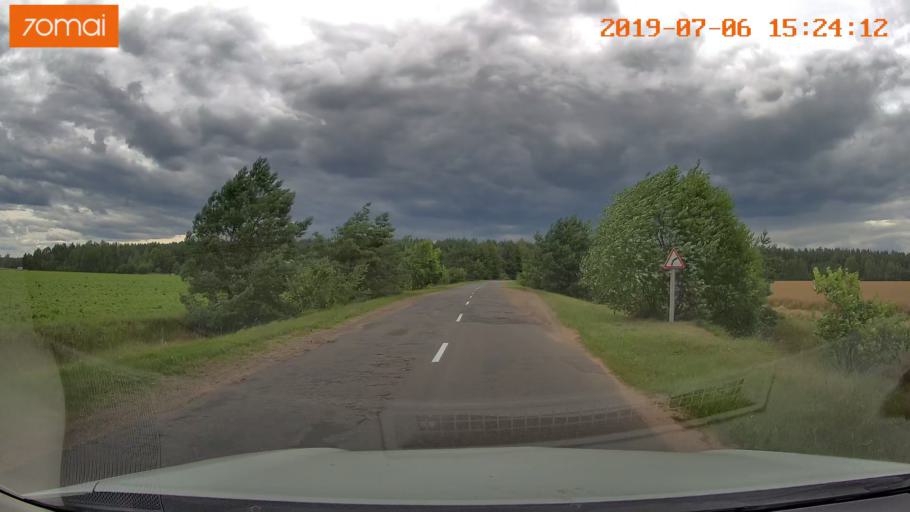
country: BY
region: Minsk
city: Valozhyn
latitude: 54.0179
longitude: 26.6033
